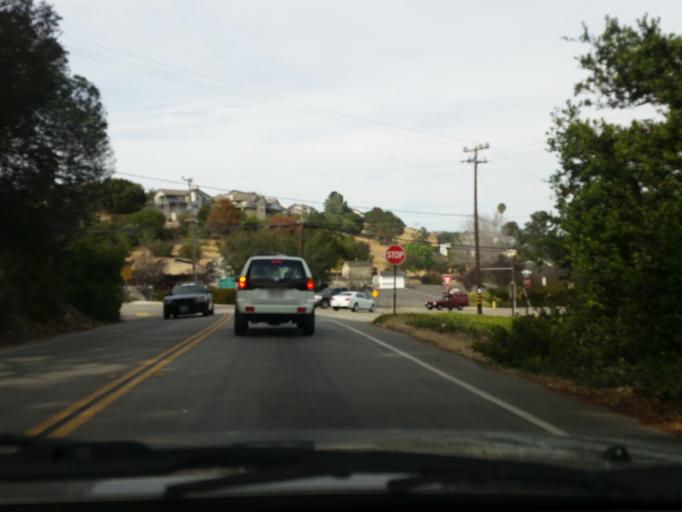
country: US
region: California
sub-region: San Luis Obispo County
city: Arroyo Grande
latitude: 35.1269
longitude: -120.5701
